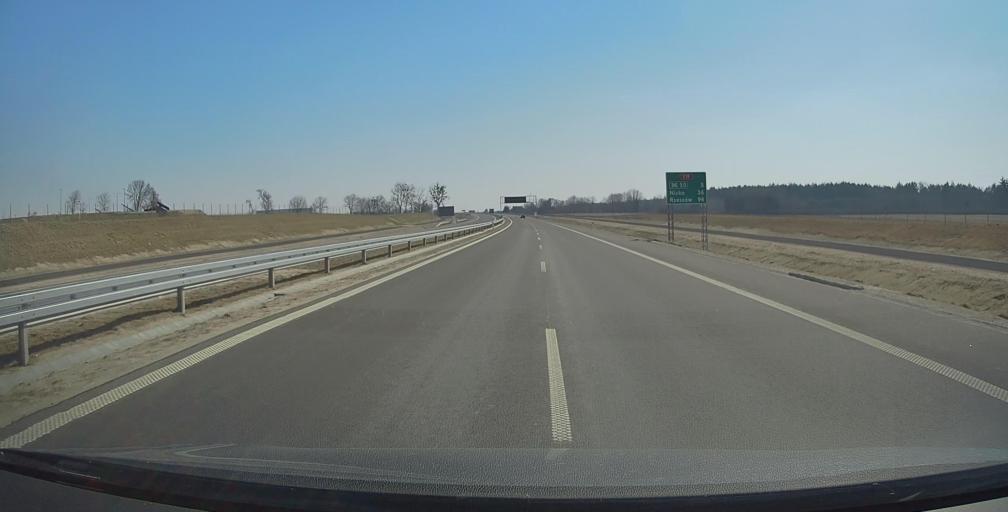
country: PL
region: Lublin Voivodeship
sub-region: Powiat janowski
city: Modliborzyce
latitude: 50.7254
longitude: 22.3617
